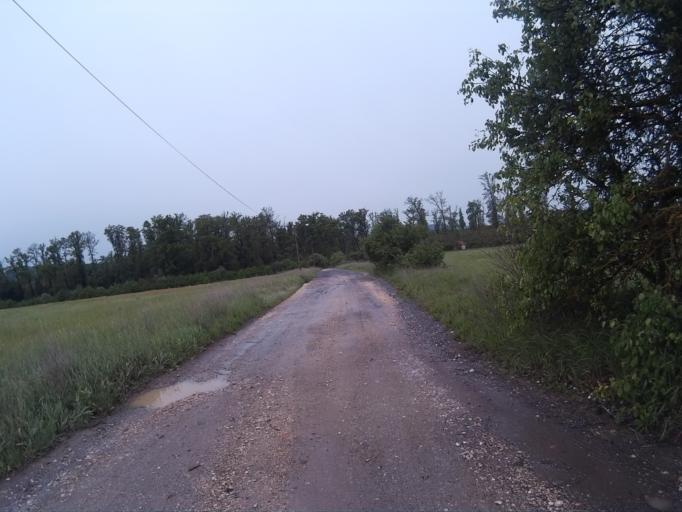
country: HU
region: Veszprem
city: Sumeg
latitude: 46.9516
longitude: 17.2899
